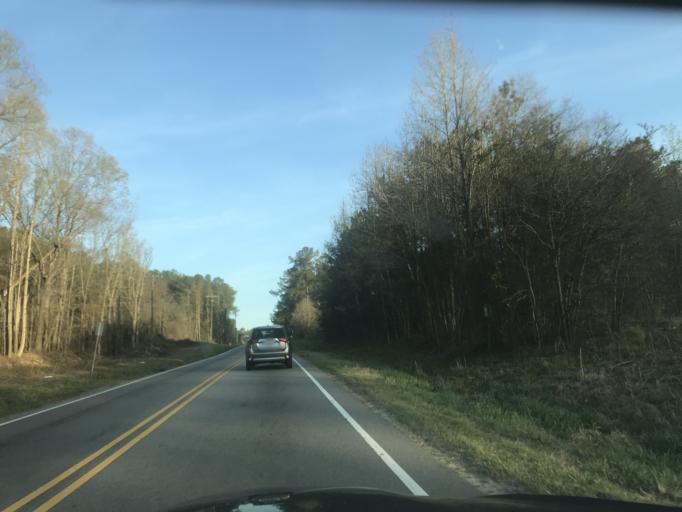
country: US
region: North Carolina
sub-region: Wake County
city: Garner
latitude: 35.7368
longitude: -78.5654
